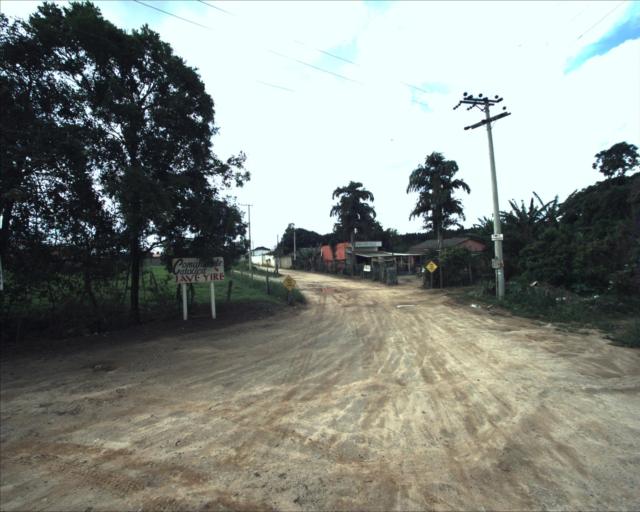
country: BR
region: Sao Paulo
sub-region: Aracoiaba Da Serra
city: Aracoiaba da Serra
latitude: -23.5524
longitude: -47.5458
